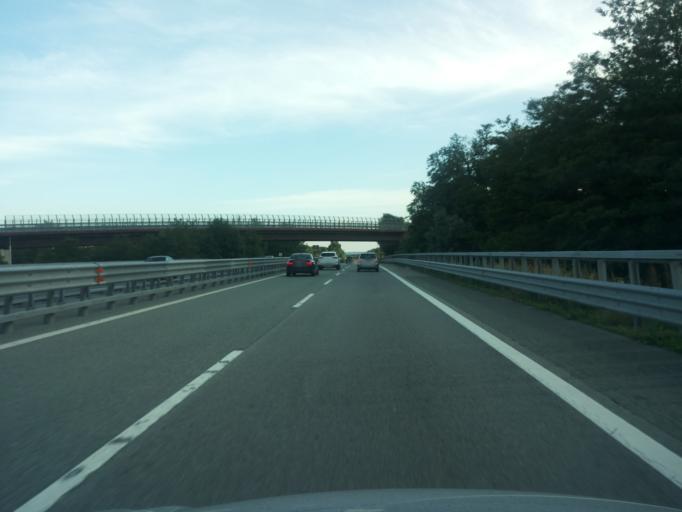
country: IT
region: Piedmont
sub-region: Provincia di Torino
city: Quassolo
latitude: 45.5019
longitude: 7.8315
